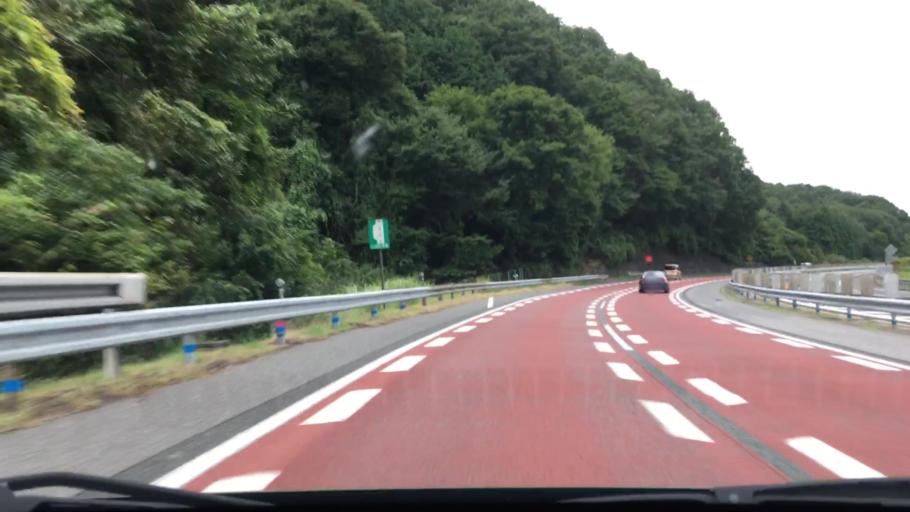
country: JP
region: Hiroshima
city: Miyoshi
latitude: 34.7796
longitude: 132.8435
